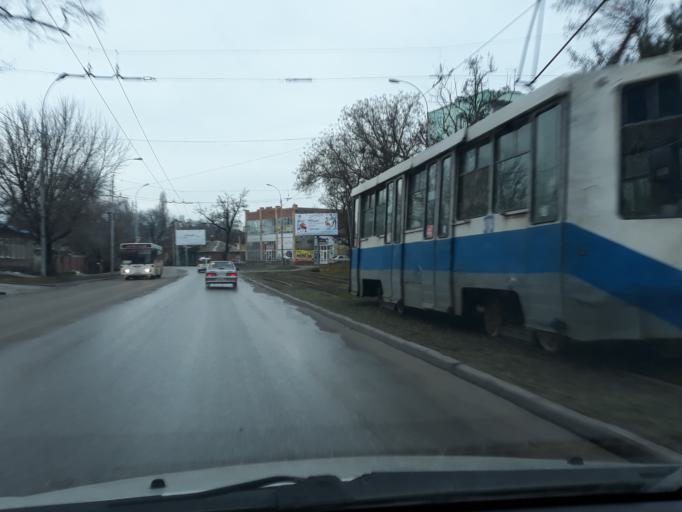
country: RU
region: Rostov
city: Taganrog
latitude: 47.2276
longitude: 38.9176
